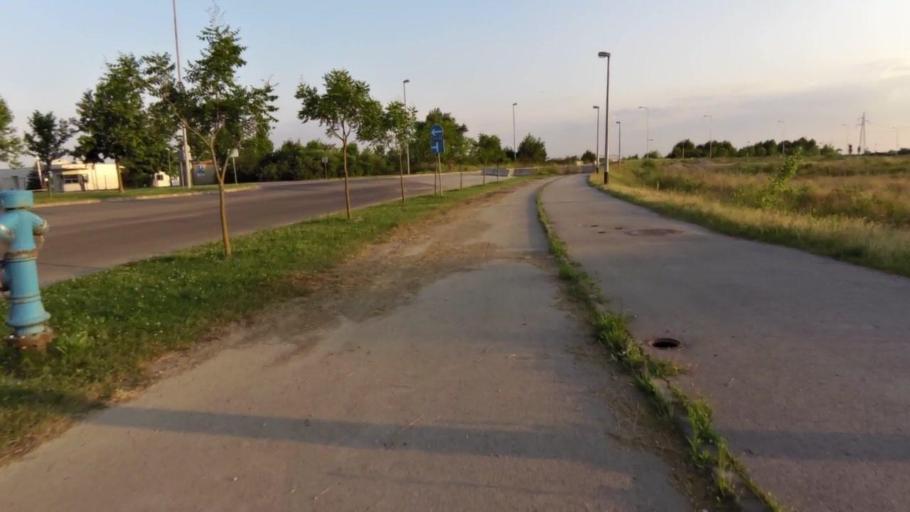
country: HR
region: Zagrebacka
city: Micevec
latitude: 45.7882
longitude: 16.0790
